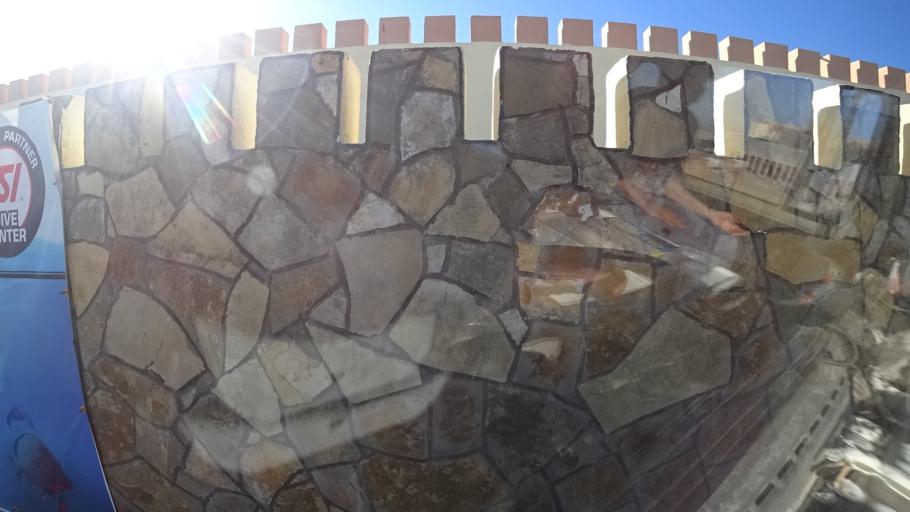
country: OM
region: Zufar
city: Salalah
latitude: 16.9757
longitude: 54.6927
